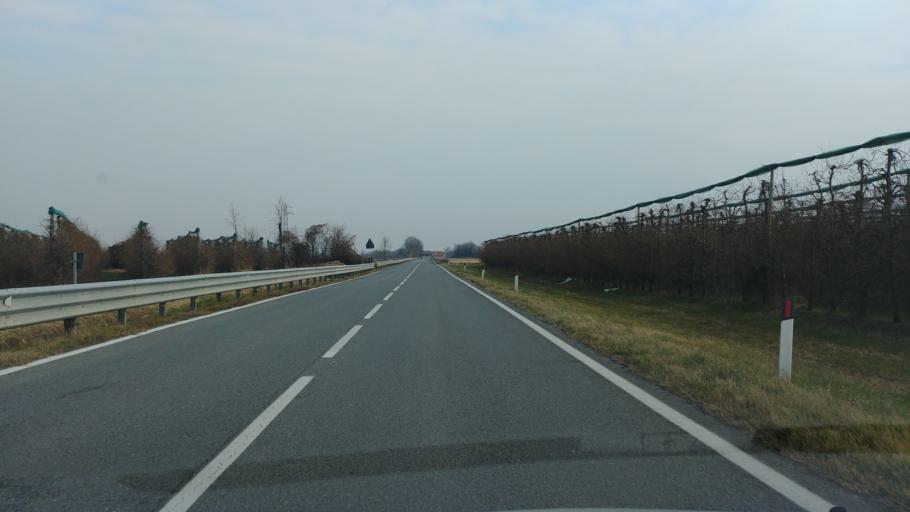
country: IT
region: Piedmont
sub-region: Provincia di Cuneo
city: Castelletto Stura
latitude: 44.4435
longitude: 7.6070
